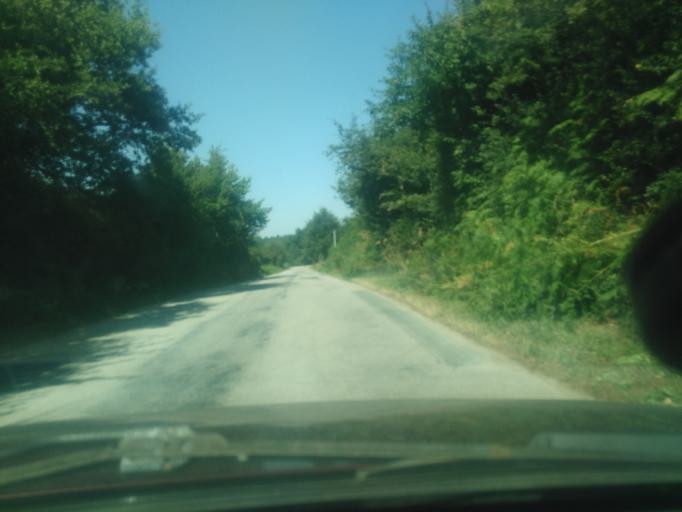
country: FR
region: Pays de la Loire
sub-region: Departement de la Vendee
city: Dompierre-sur-Yon
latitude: 46.7205
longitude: -1.3942
